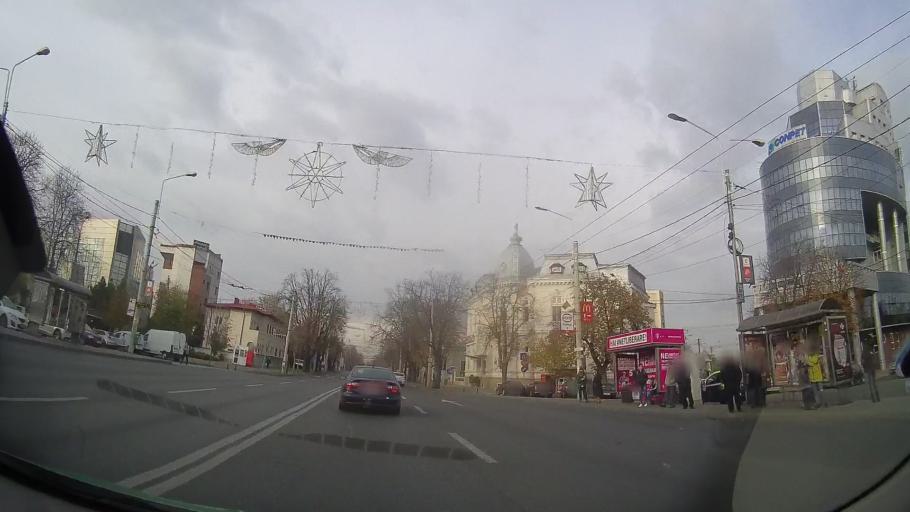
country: RO
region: Prahova
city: Ploiesti
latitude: 44.9334
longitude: 26.0270
